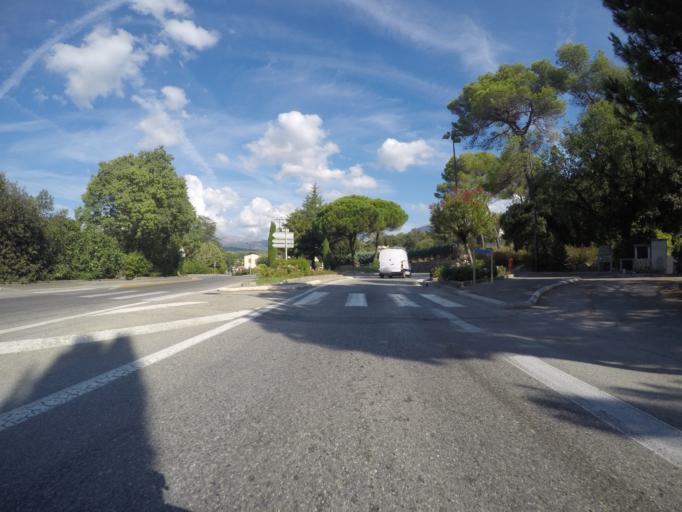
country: FR
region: Provence-Alpes-Cote d'Azur
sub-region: Departement des Alpes-Maritimes
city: Le Rouret
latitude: 43.6646
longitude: 7.0533
